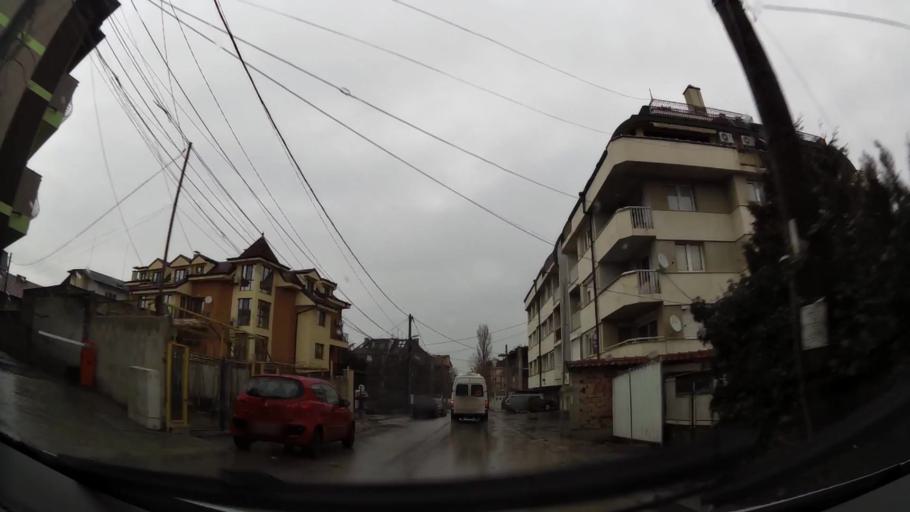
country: BG
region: Sofia-Capital
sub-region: Stolichna Obshtina
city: Sofia
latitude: 42.6463
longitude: 23.3336
